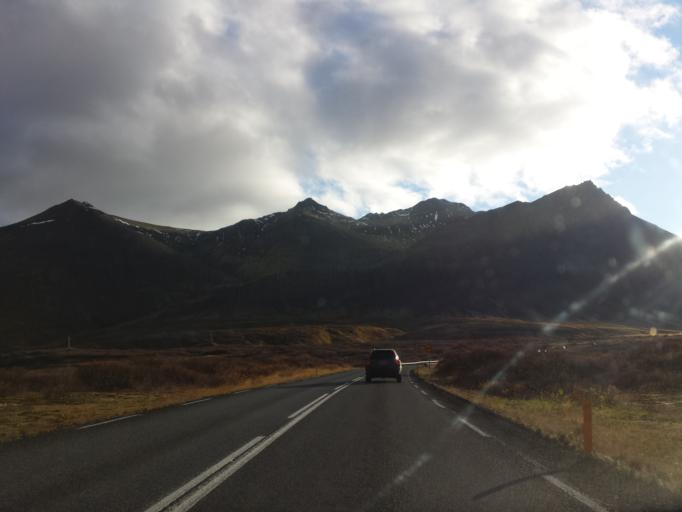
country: IS
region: West
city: Borgarnes
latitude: 64.5197
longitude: -21.8866
